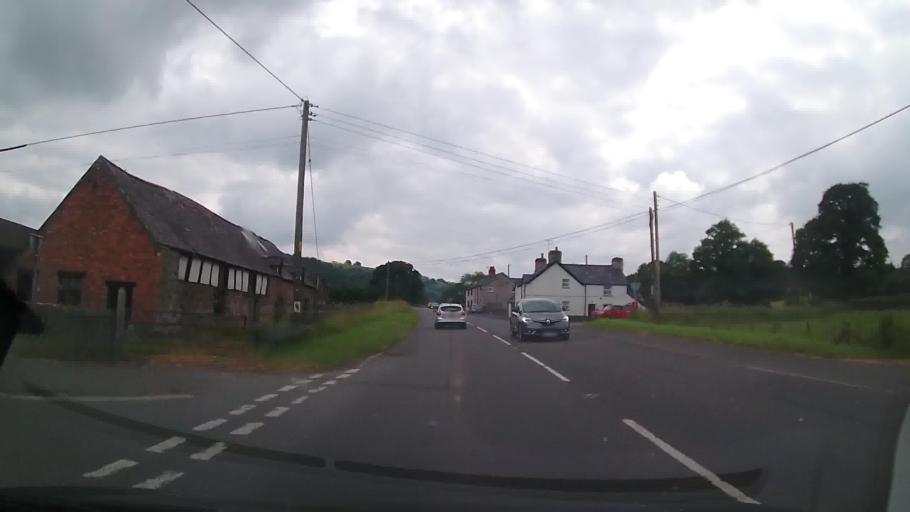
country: GB
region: Wales
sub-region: Denbighshire
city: Llandrillo
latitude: 52.9755
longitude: -3.4405
